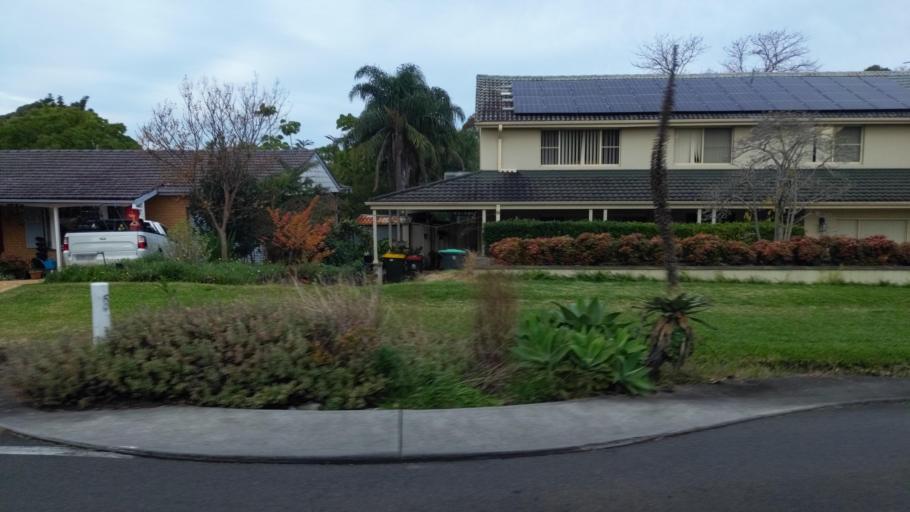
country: AU
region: New South Wales
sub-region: The Hills Shire
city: Baulkham Hills
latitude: -33.7510
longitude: 150.9619
